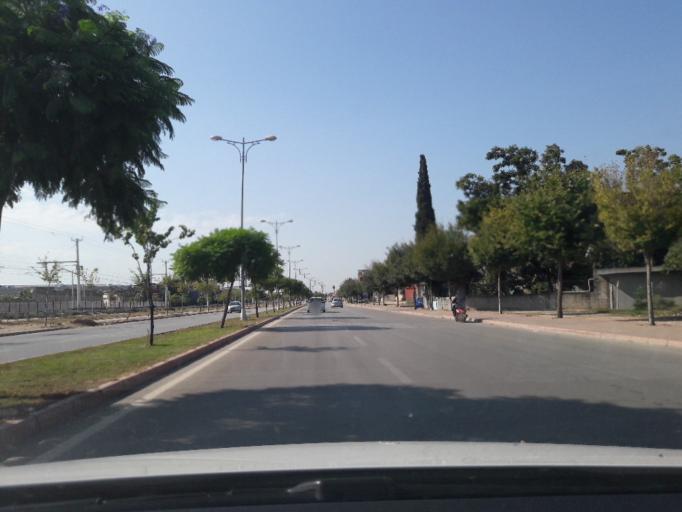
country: TR
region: Adana
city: Seyhan
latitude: 37.0002
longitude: 35.3061
